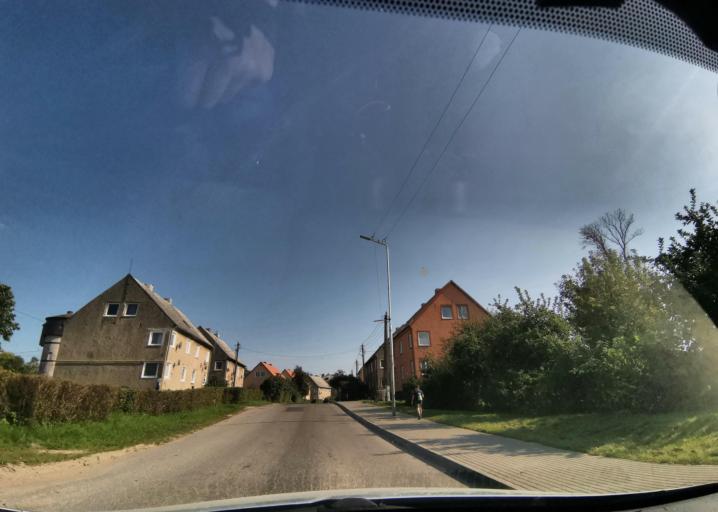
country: RU
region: Kaliningrad
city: Neman
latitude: 55.0337
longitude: 22.0375
